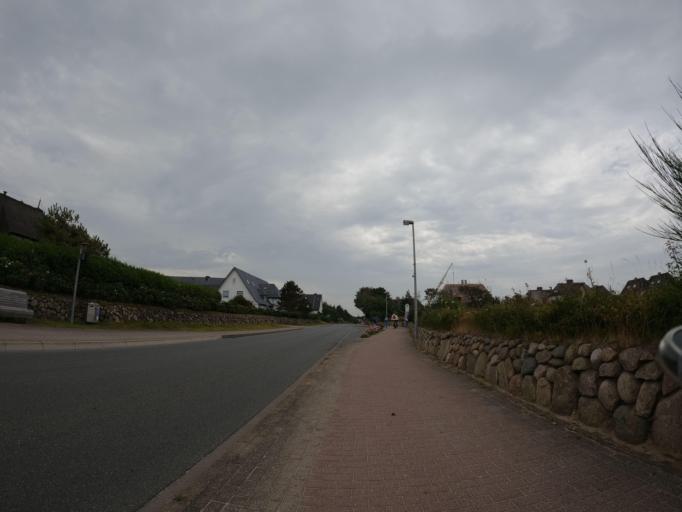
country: DE
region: Schleswig-Holstein
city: Westerland
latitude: 54.9295
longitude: 8.3188
